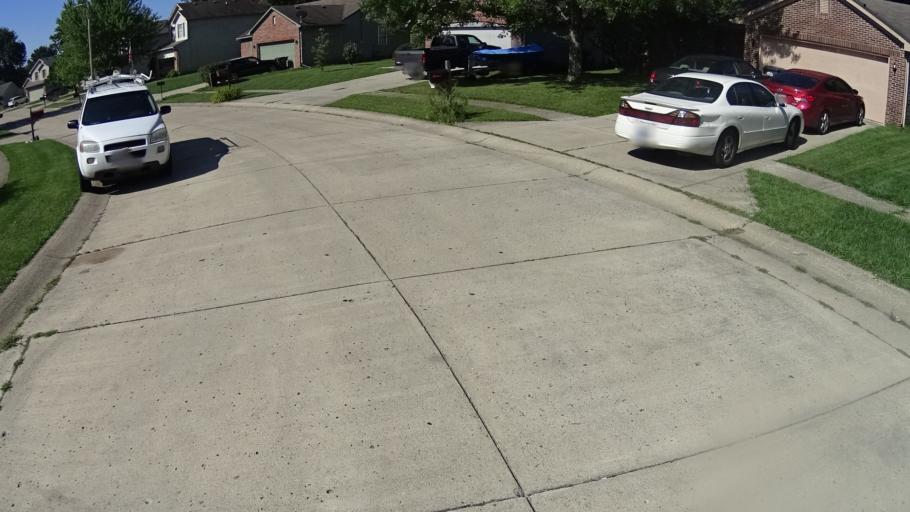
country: US
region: Indiana
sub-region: Madison County
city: Pendleton
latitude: 40.0061
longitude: -85.7356
